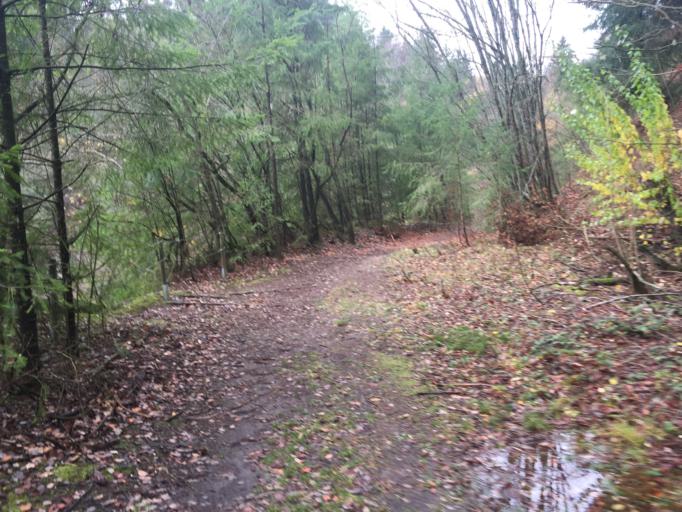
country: DE
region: Baden-Wuerttemberg
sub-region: Karlsruhe Region
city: Zwingenberg
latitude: 49.4697
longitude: 9.0456
